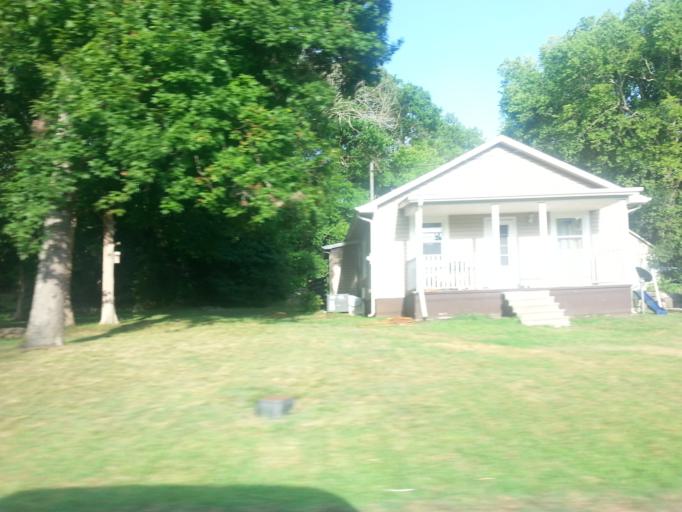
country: US
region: Tennessee
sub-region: Blount County
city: Louisville
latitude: 35.7703
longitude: -84.1316
